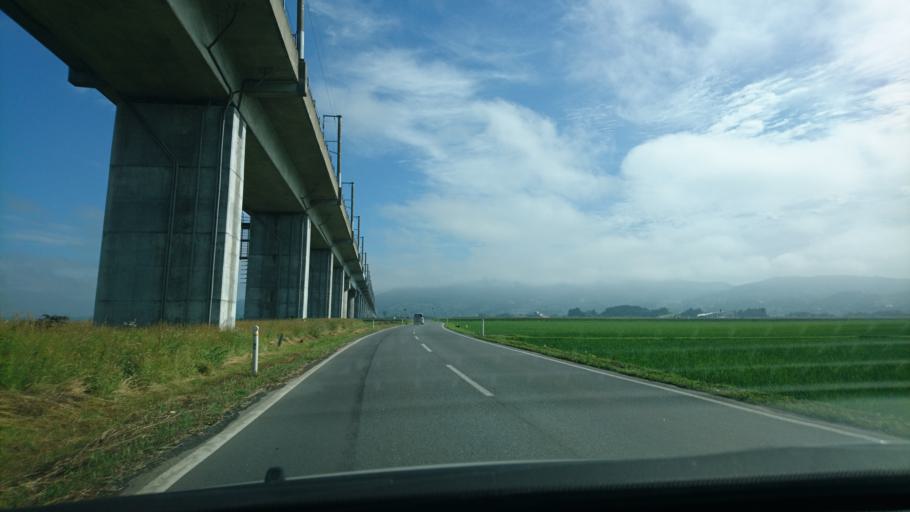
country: JP
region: Iwate
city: Ichinoseki
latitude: 38.9460
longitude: 141.1472
